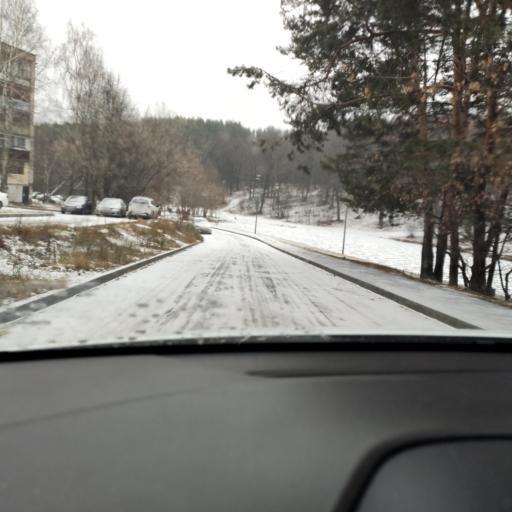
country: RU
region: Tatarstan
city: Vysokaya Gora
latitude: 55.8581
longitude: 49.2284
